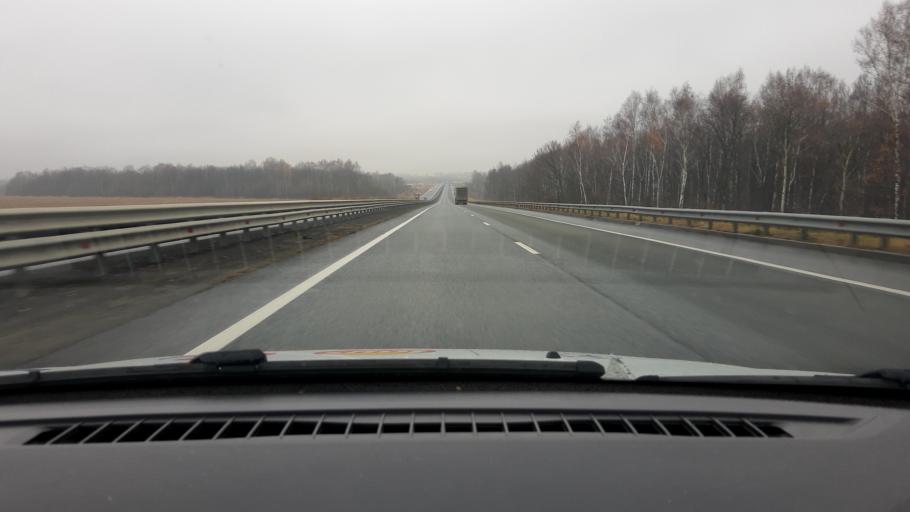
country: RU
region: Nizjnij Novgorod
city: Burevestnik
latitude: 56.1368
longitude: 43.7689
